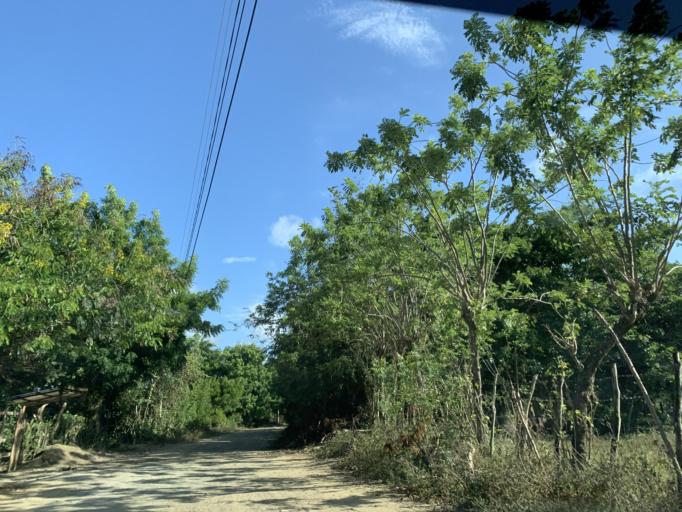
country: DO
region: Puerto Plata
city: Luperon
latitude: 19.8979
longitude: -70.8795
